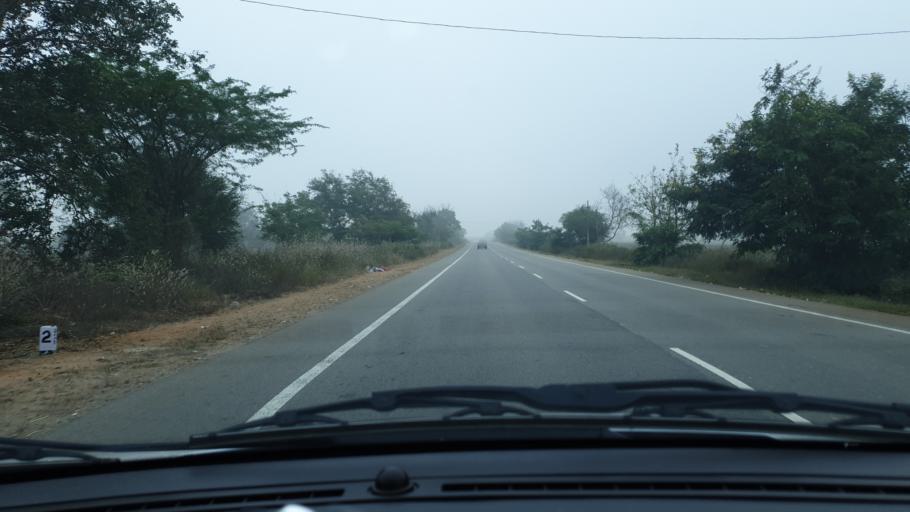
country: IN
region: Telangana
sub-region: Nalgonda
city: Devarkonda
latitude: 16.6341
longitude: 78.6393
